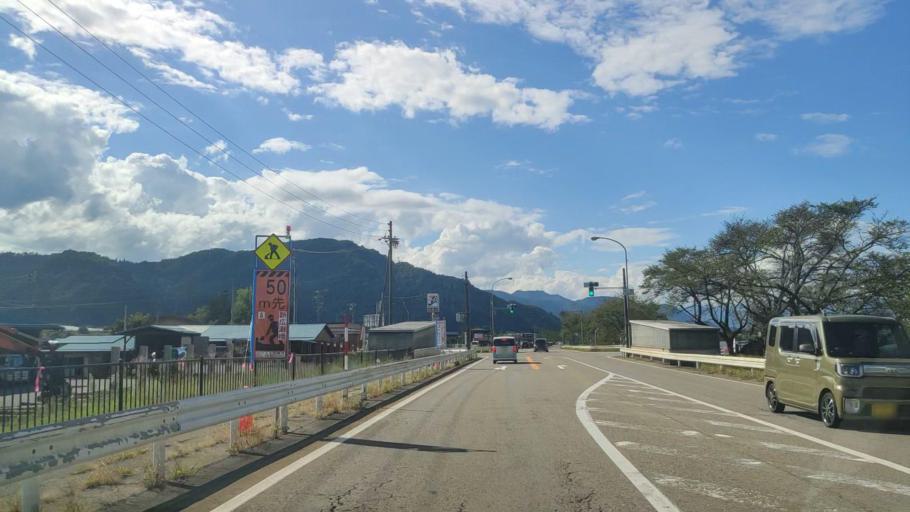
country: JP
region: Gifu
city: Takayama
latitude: 36.2065
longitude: 137.2202
